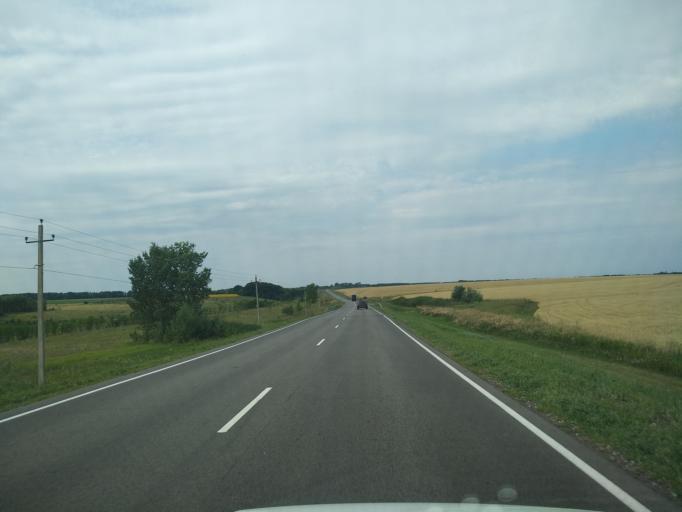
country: RU
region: Voronezj
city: Pereleshinskiy
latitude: 51.8221
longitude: 40.2716
